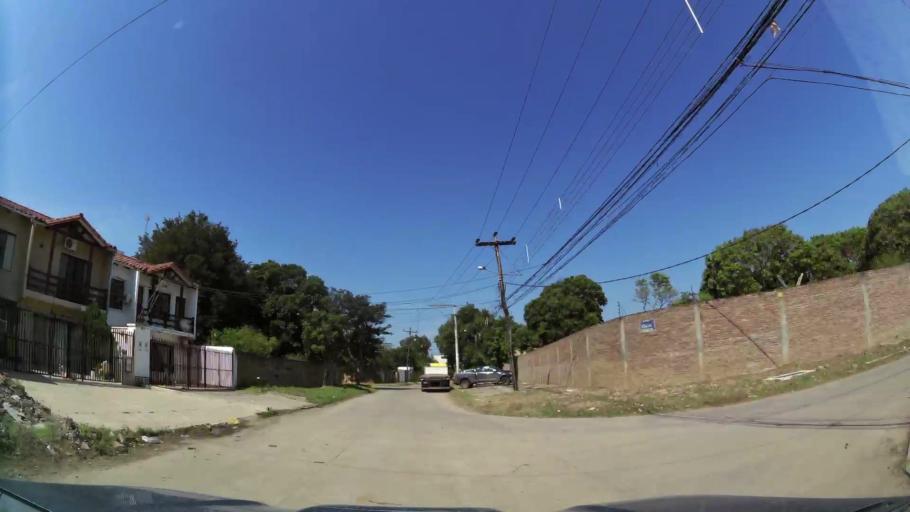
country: BO
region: Santa Cruz
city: Santa Cruz de la Sierra
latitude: -17.7478
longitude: -63.1729
